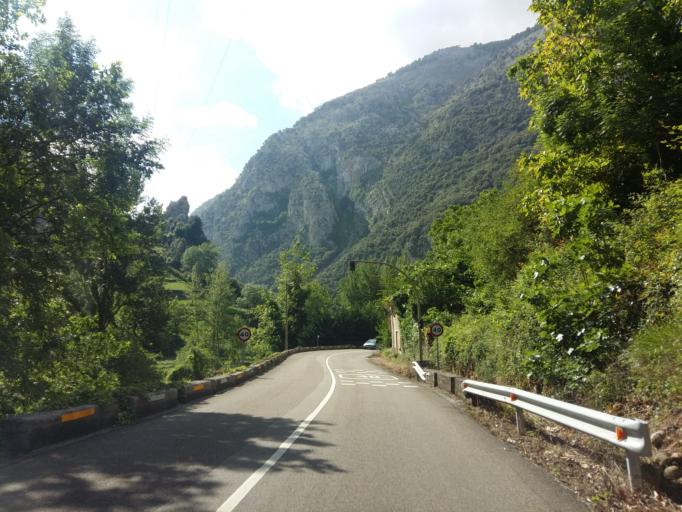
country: ES
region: Cantabria
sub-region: Provincia de Cantabria
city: Tresviso
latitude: 43.2572
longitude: -4.6163
